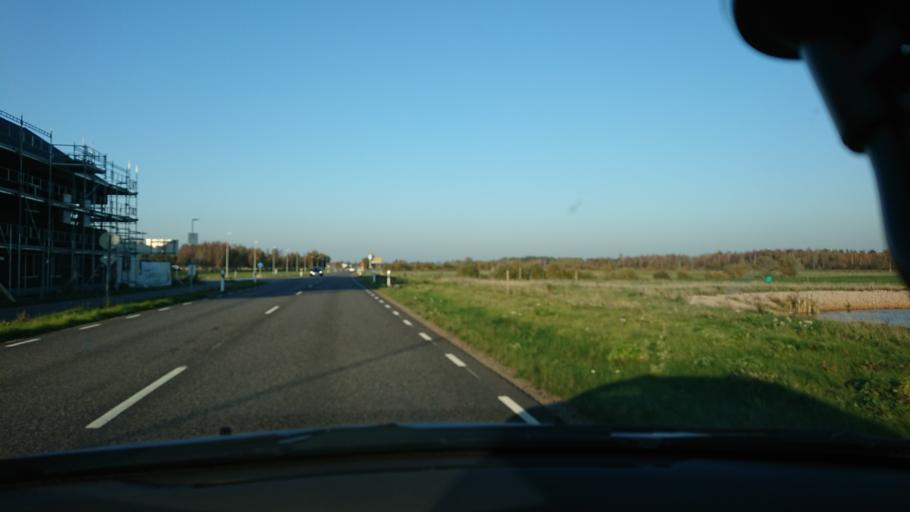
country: SE
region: Halland
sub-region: Laholms Kommun
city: Mellbystrand
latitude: 56.4464
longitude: 12.9302
